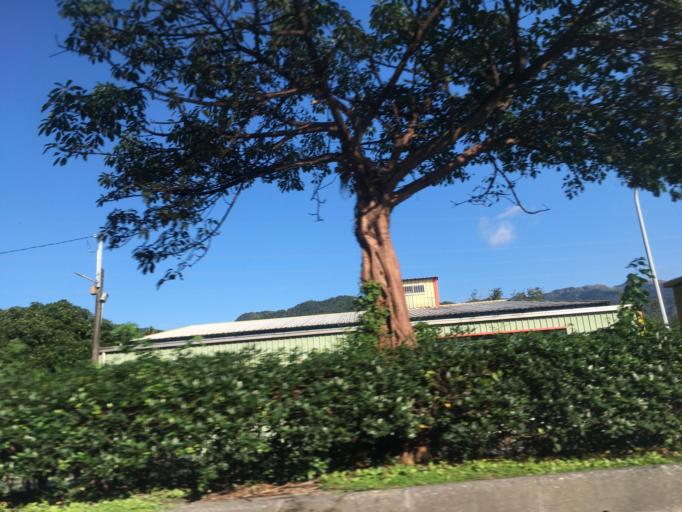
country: TW
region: Taiwan
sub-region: Yilan
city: Yilan
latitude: 24.8412
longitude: 121.8013
